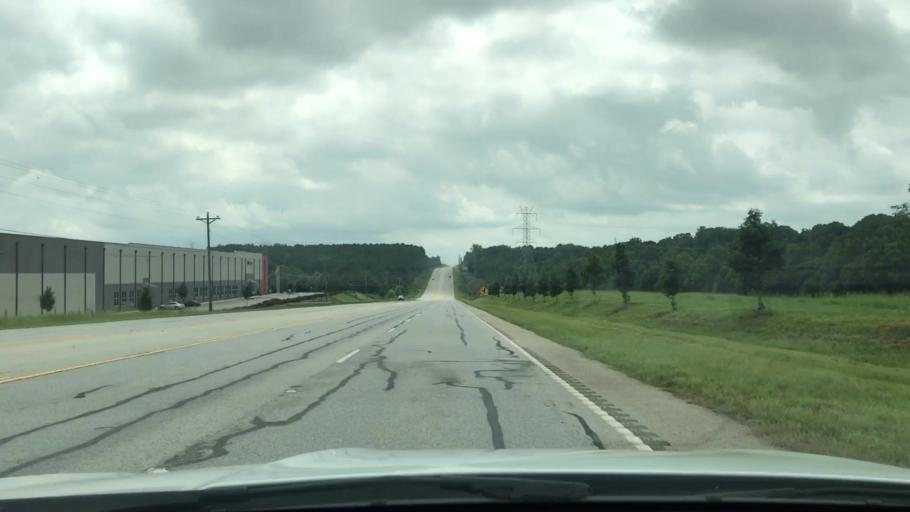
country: US
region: South Carolina
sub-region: Spartanburg County
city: Roebuck
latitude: 34.8677
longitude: -82.0303
